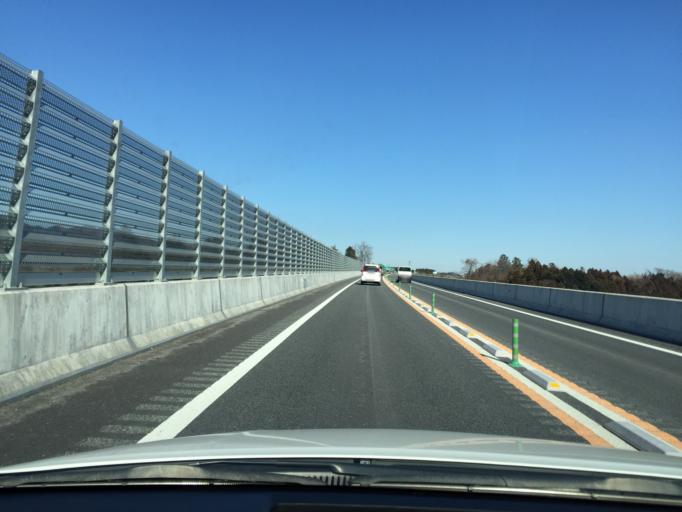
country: JP
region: Fukushima
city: Namie
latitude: 37.5978
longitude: 140.9260
